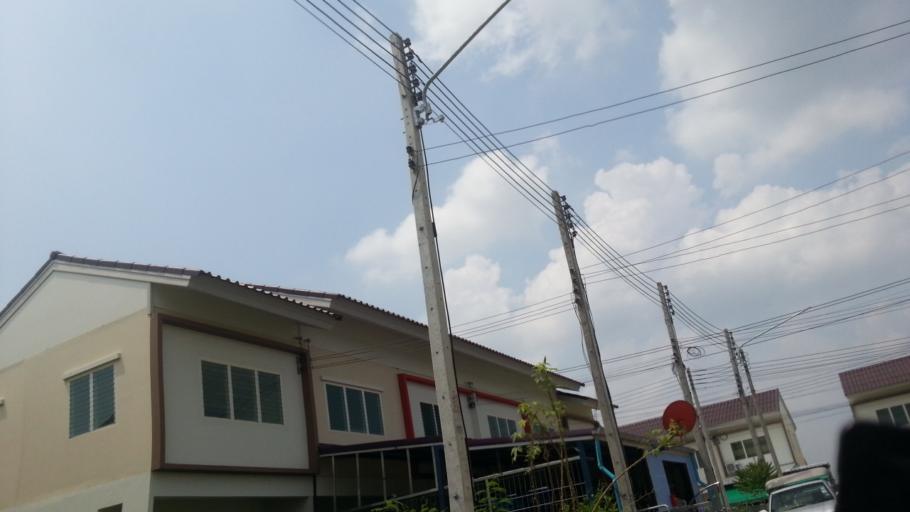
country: TH
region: Pathum Thani
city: Nong Suea
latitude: 14.0645
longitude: 100.8228
